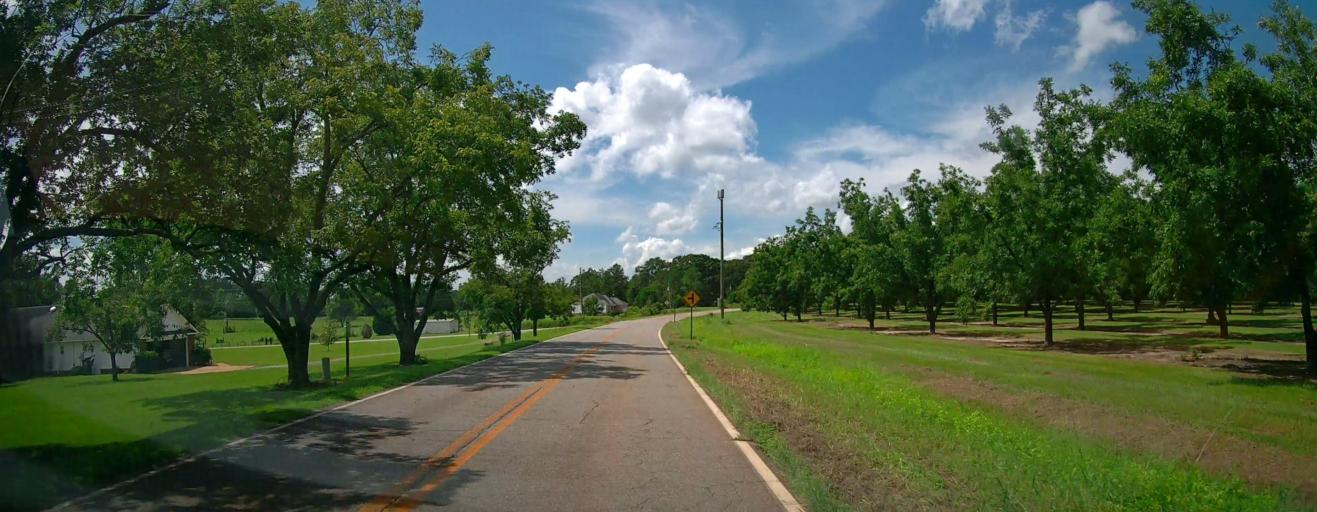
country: US
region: Georgia
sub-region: Houston County
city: Perry
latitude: 32.5212
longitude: -83.7956
